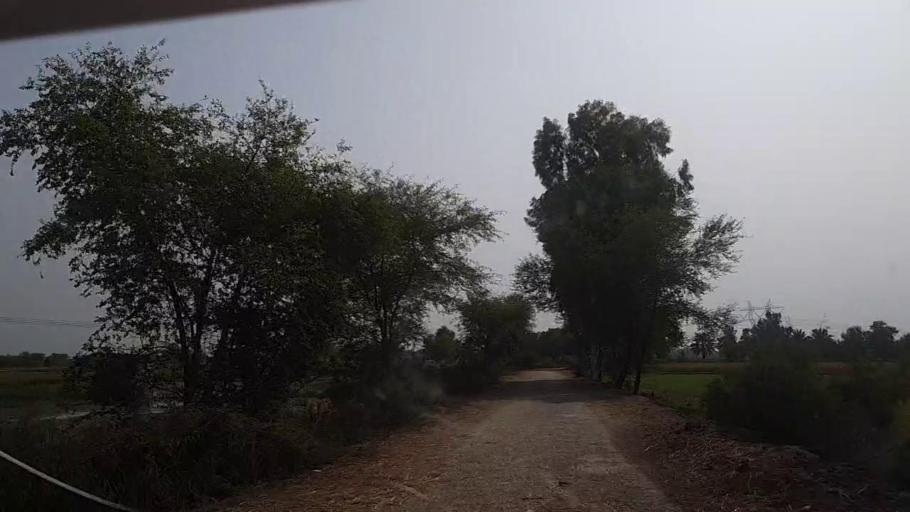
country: PK
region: Sindh
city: Madeji
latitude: 27.7408
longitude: 68.4359
